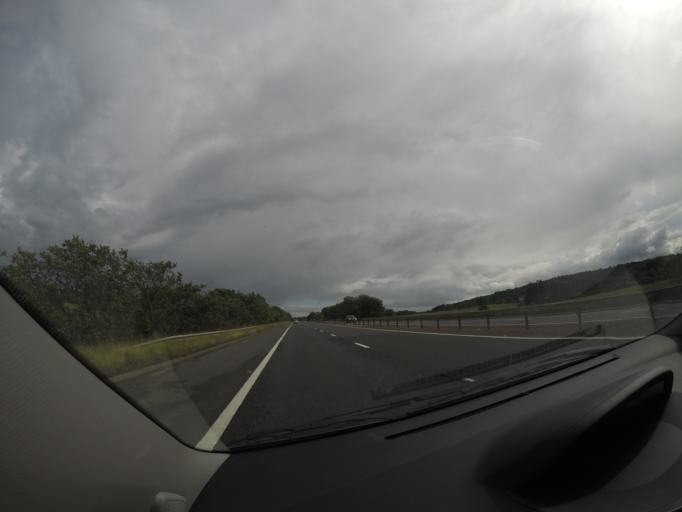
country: GB
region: Scotland
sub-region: Falkirk
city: Dunipace
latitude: 56.0520
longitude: -3.9213
